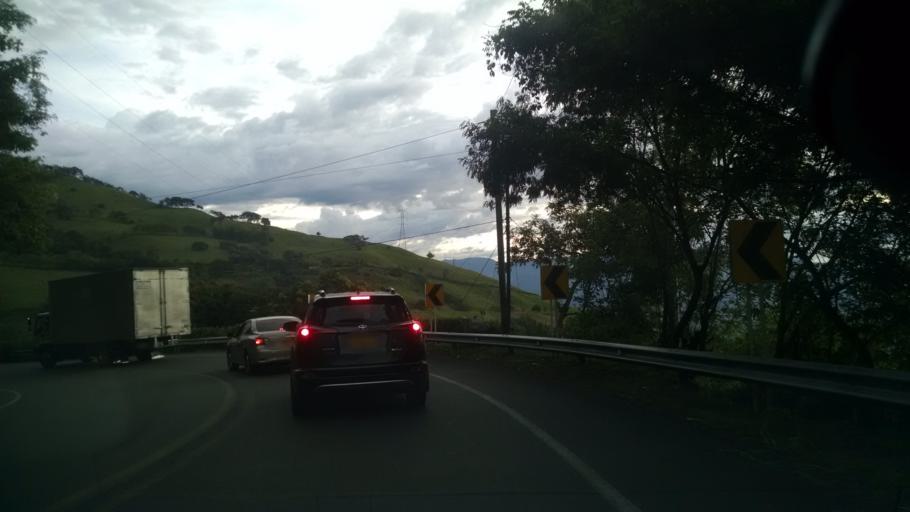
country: CO
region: Antioquia
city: Santa Barbara
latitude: 5.8381
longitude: -75.5844
